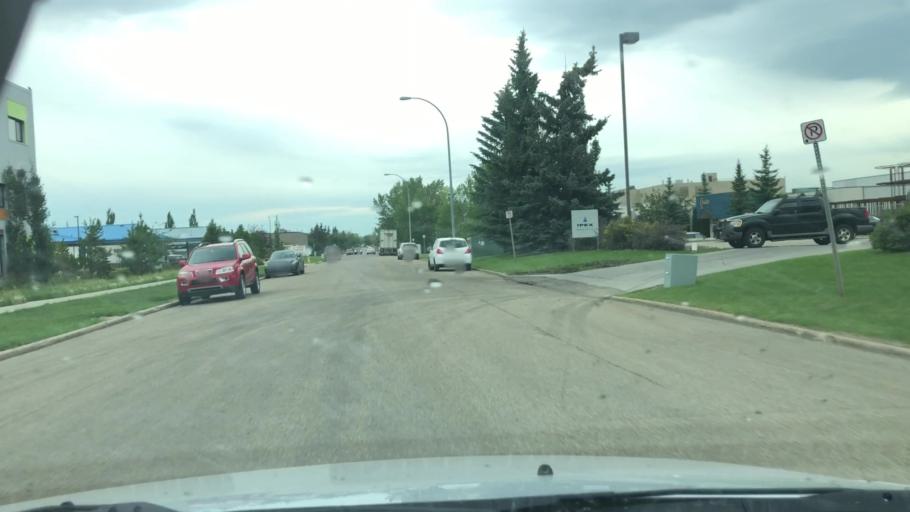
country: CA
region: Alberta
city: Edmonton
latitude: 53.5285
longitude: -113.4149
